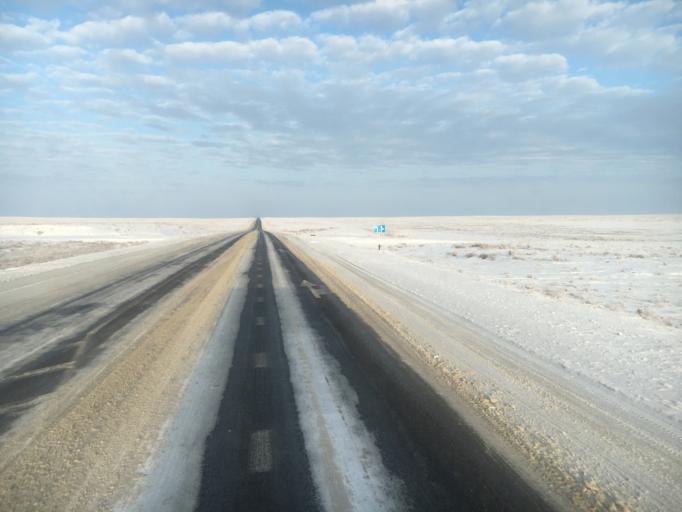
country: KZ
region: Qyzylorda
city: Sekseuil
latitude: 47.6795
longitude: 61.4424
